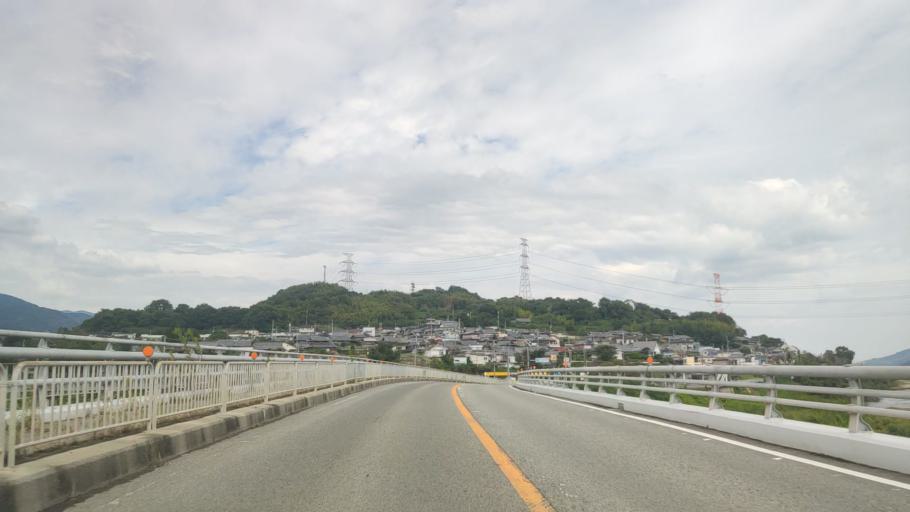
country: JP
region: Wakayama
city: Iwade
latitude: 34.2789
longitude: 135.4477
